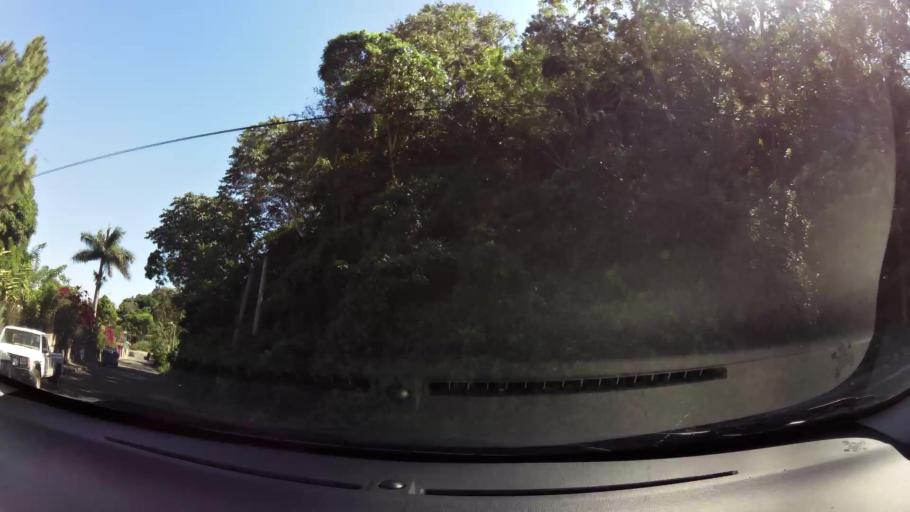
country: SV
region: La Libertad
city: Santa Tecla
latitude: 13.6710
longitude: -89.3022
